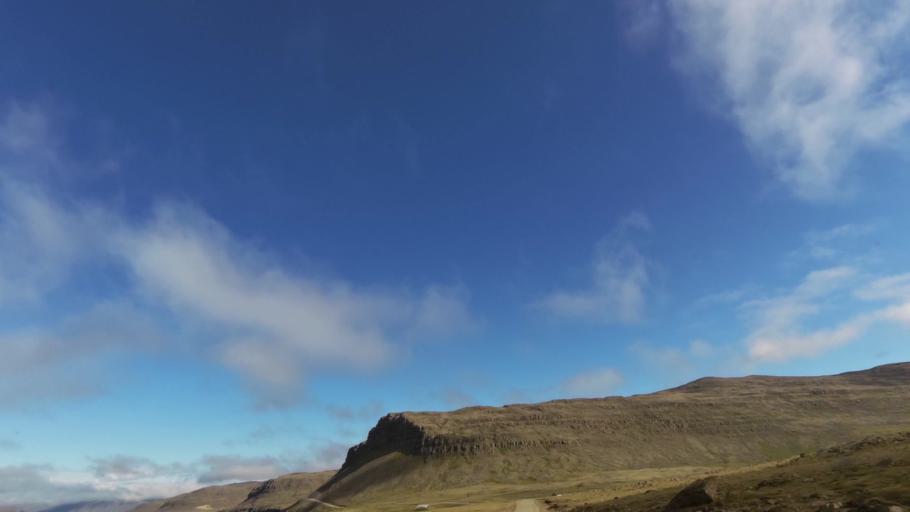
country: IS
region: West
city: Olafsvik
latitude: 65.5745
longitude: -24.0655
